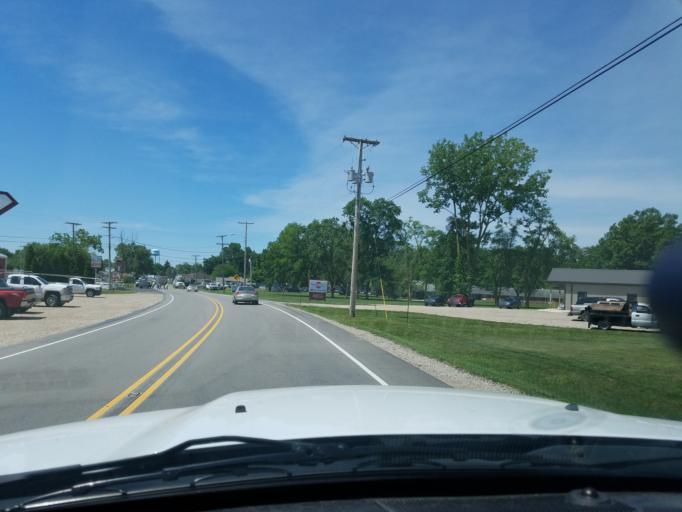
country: US
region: Indiana
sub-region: Delaware County
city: Albany
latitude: 40.3031
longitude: -85.2447
